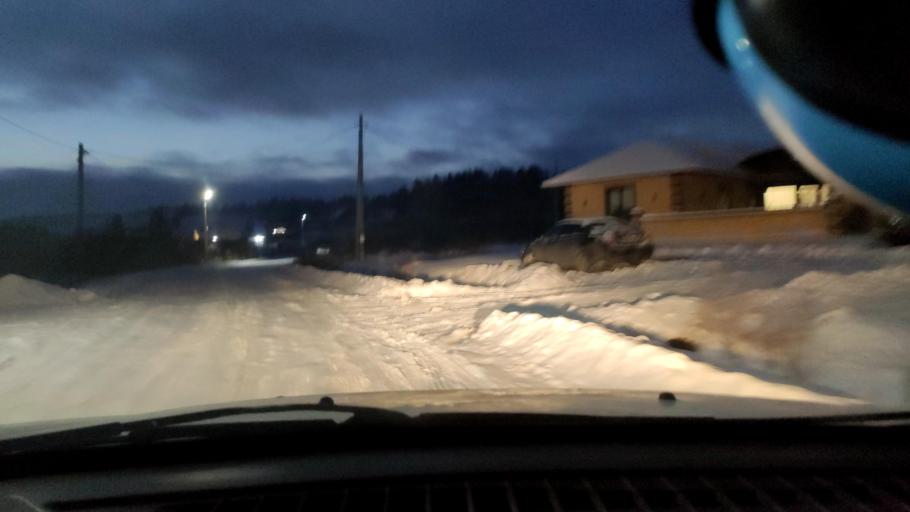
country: RU
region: Perm
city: Kultayevo
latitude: 57.9221
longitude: 55.8667
